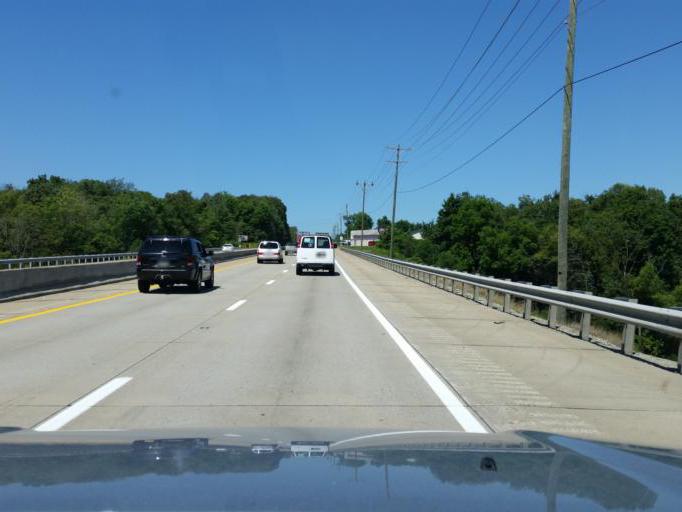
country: US
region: Pennsylvania
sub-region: Westmoreland County
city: Delmont
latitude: 40.4087
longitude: -79.6136
